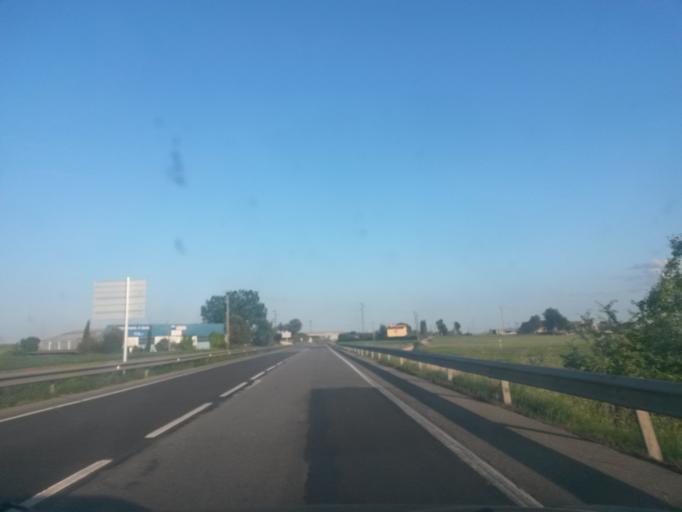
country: ES
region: Catalonia
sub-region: Provincia de Girona
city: Banyoles
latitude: 42.1384
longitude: 2.7679
